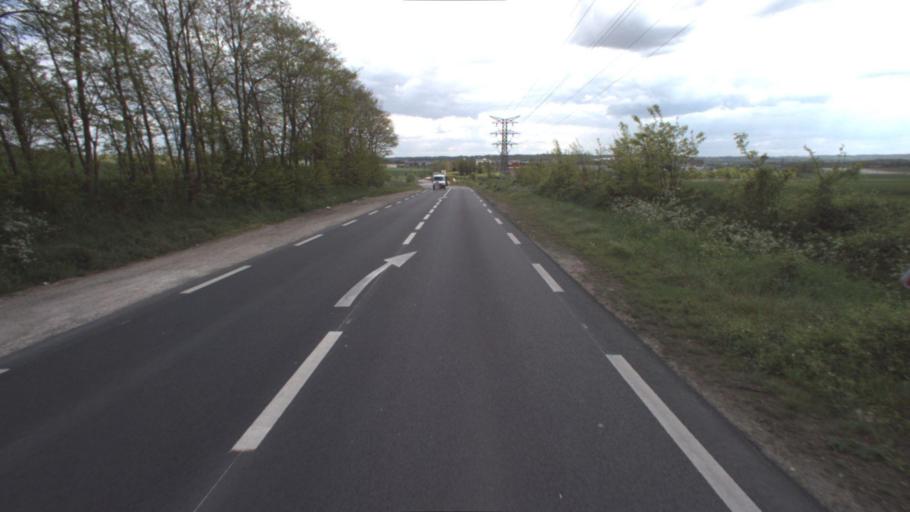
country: FR
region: Ile-de-France
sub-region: Departement de Seine-et-Marne
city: Chauconin-Neufmontiers
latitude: 48.9654
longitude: 2.8598
